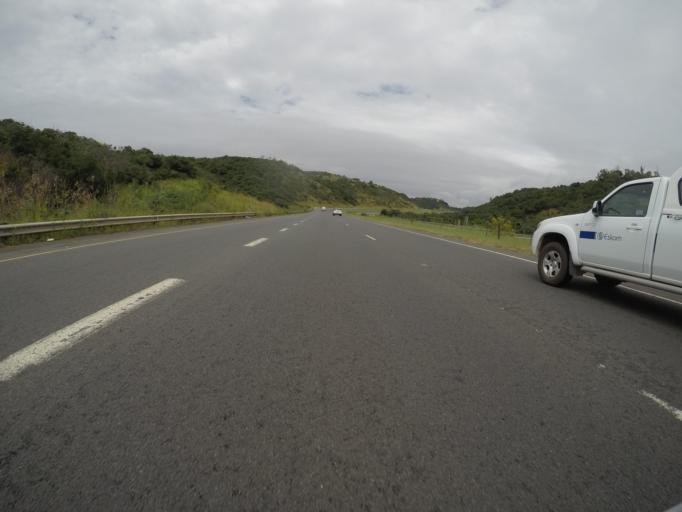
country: ZA
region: Eastern Cape
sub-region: Buffalo City Metropolitan Municipality
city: East London
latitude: -32.9665
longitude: 27.9174
